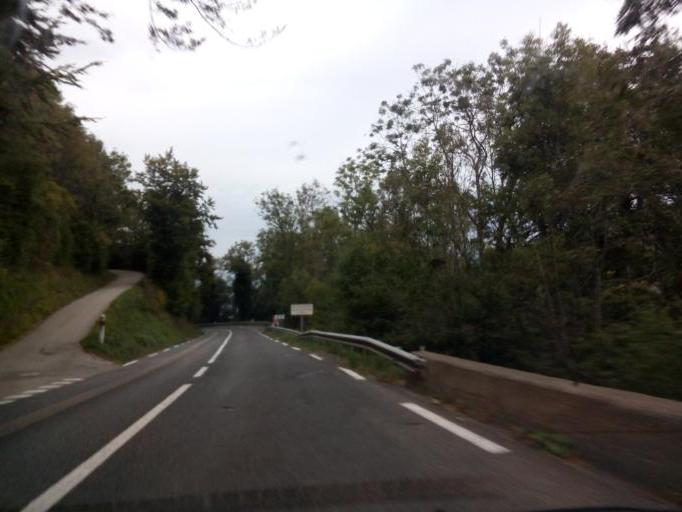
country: FR
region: Rhone-Alpes
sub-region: Departement de l'Isere
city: Notre-Dame-de-Mesage
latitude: 45.0274
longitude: 5.7719
